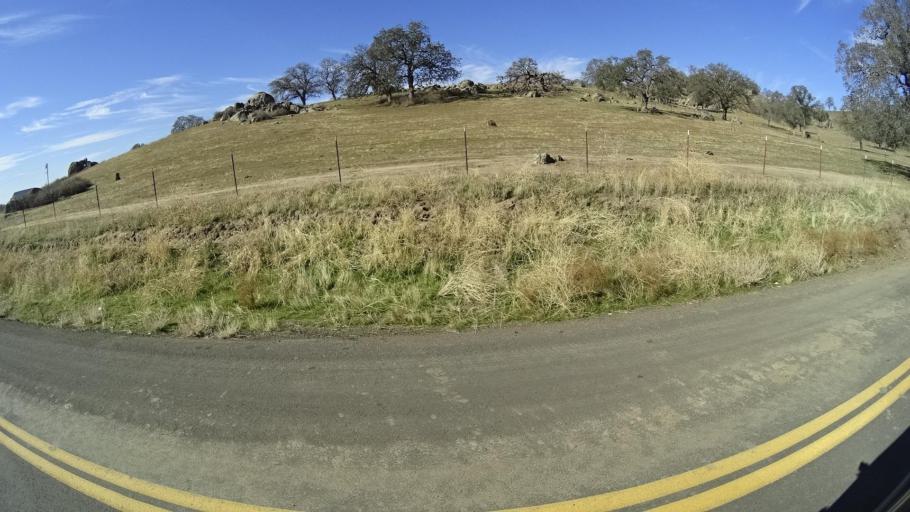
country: US
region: California
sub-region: Kern County
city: Oildale
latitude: 35.6365
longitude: -118.8383
